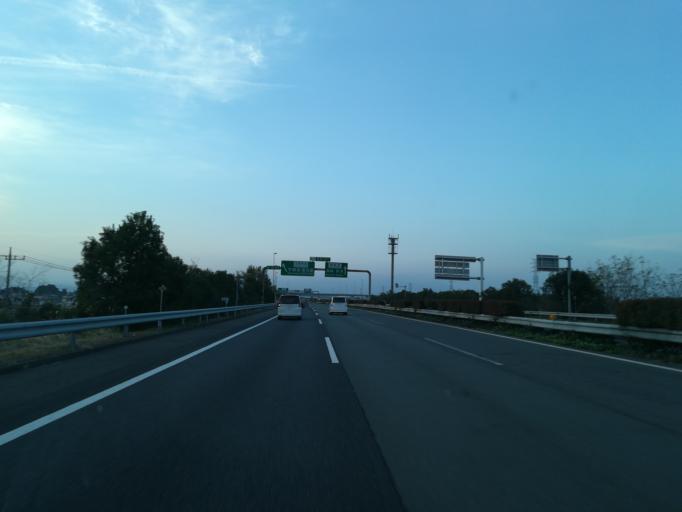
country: JP
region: Gunma
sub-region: Sawa-gun
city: Tamamura
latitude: 36.3172
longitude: 139.0812
